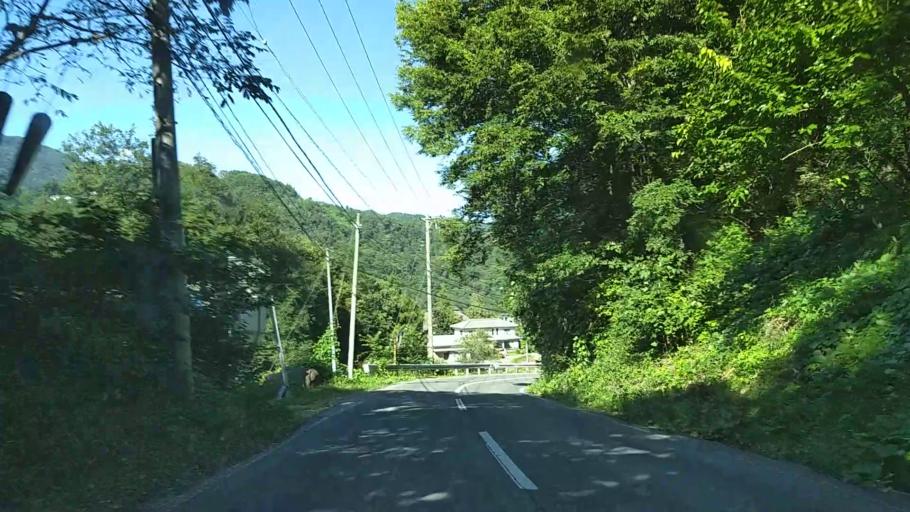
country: JP
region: Nagano
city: Nagano-shi
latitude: 36.6147
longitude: 138.0914
